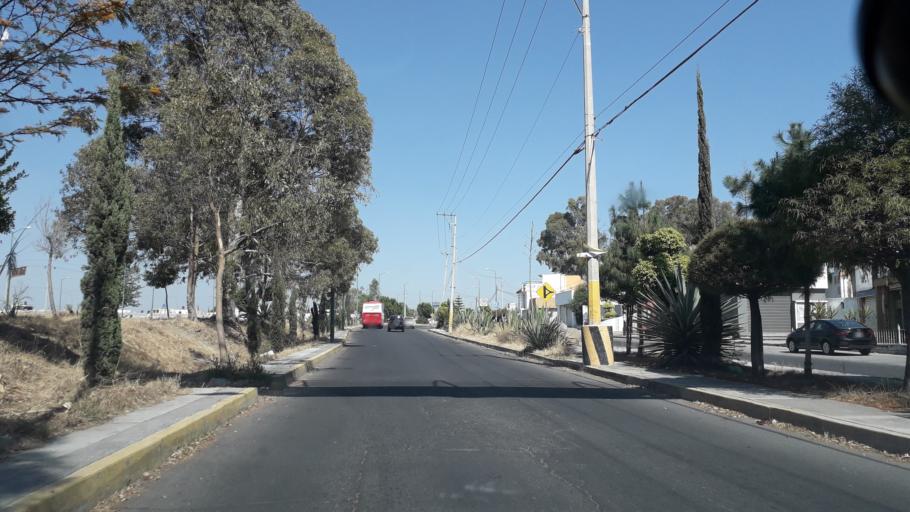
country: MX
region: Puebla
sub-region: Puebla
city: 18 de Marzo
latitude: 18.9780
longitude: -98.2169
